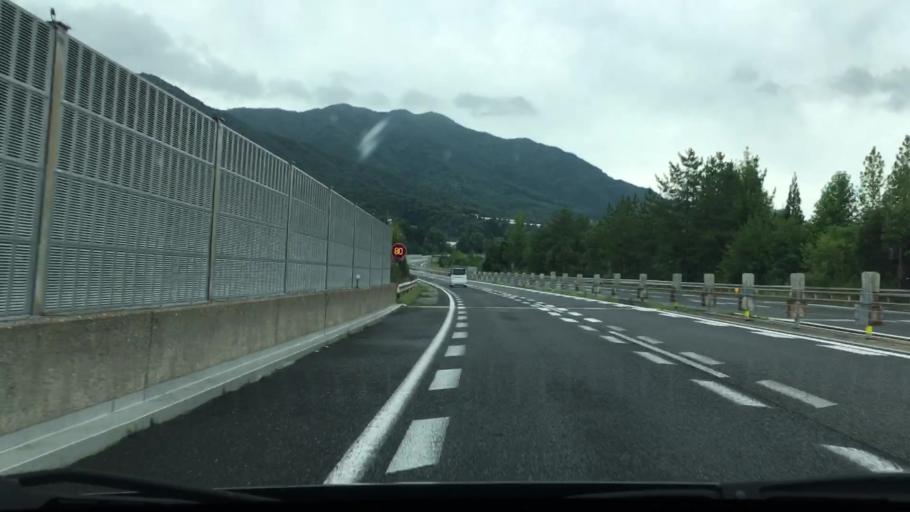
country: JP
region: Hiroshima
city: Hiroshima-shi
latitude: 34.6485
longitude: 132.5167
